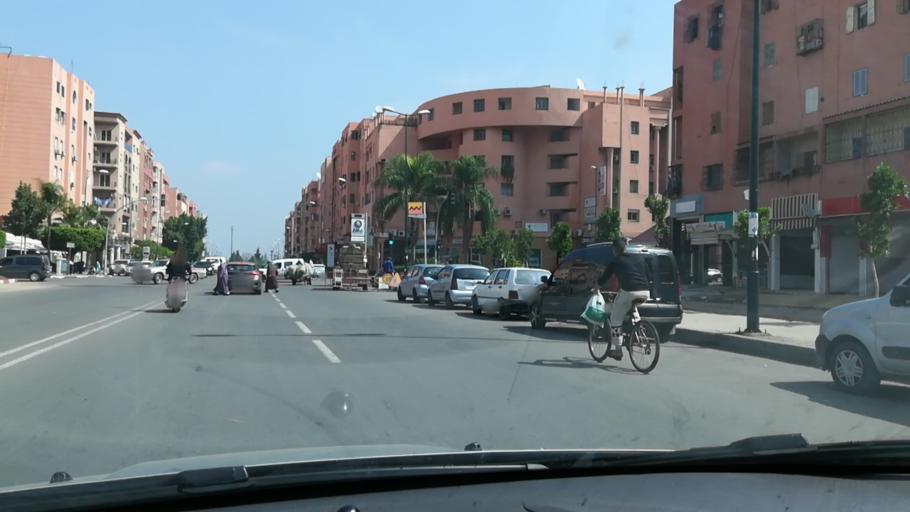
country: MA
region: Marrakech-Tensift-Al Haouz
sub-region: Marrakech
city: Marrakesh
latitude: 31.6341
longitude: -8.0582
